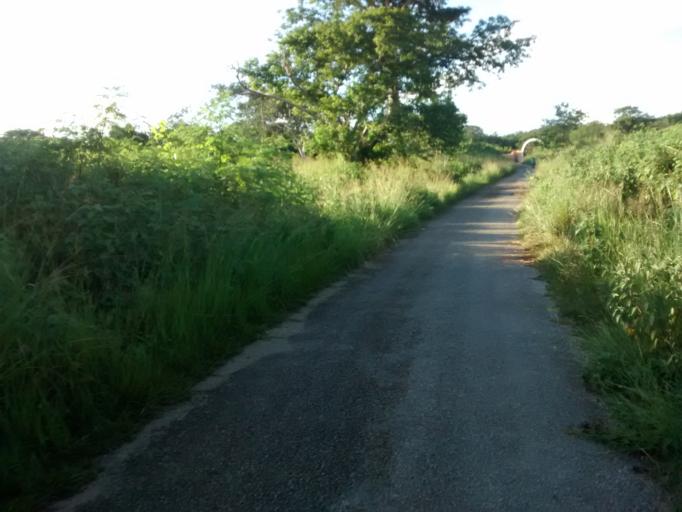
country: MX
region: Yucatan
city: Valladolid
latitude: 20.7096
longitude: -88.2163
